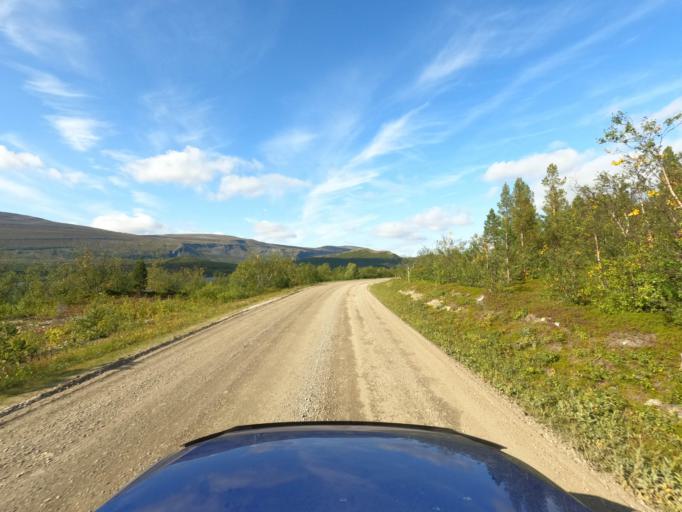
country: NO
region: Finnmark Fylke
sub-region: Porsanger
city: Lakselv
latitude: 69.8928
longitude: 24.9942
